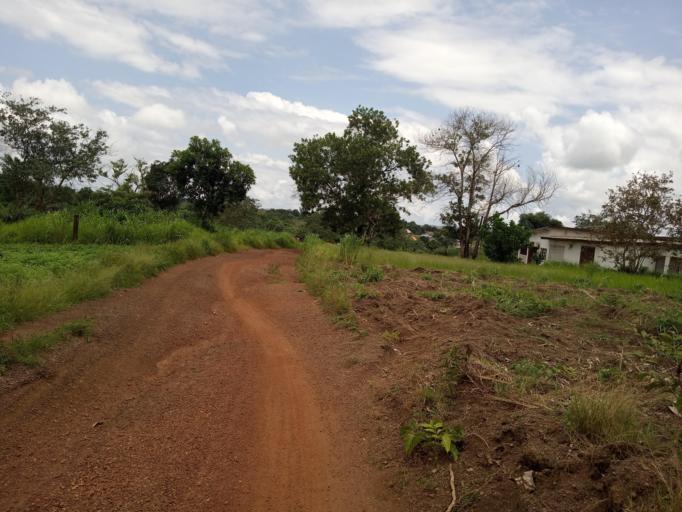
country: SL
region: Northern Province
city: Kamakwie
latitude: 9.4862
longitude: -12.2437
